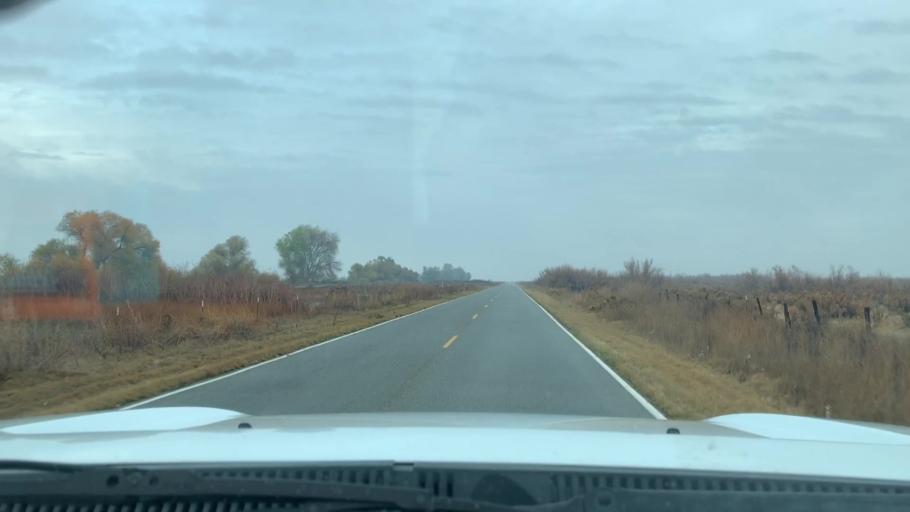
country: US
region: California
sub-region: Kern County
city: Lost Hills
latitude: 35.7264
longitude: -119.5794
